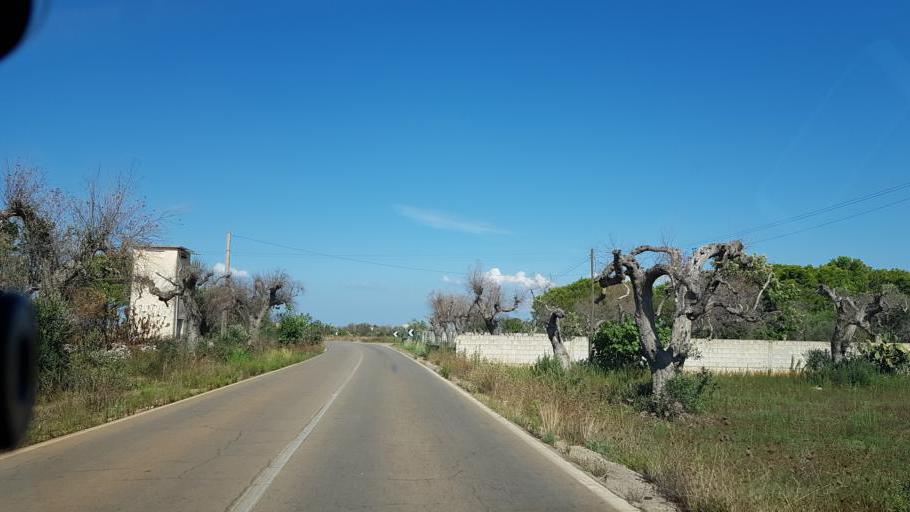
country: IT
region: Apulia
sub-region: Provincia di Lecce
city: Copertino
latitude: 40.2870
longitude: 18.0799
